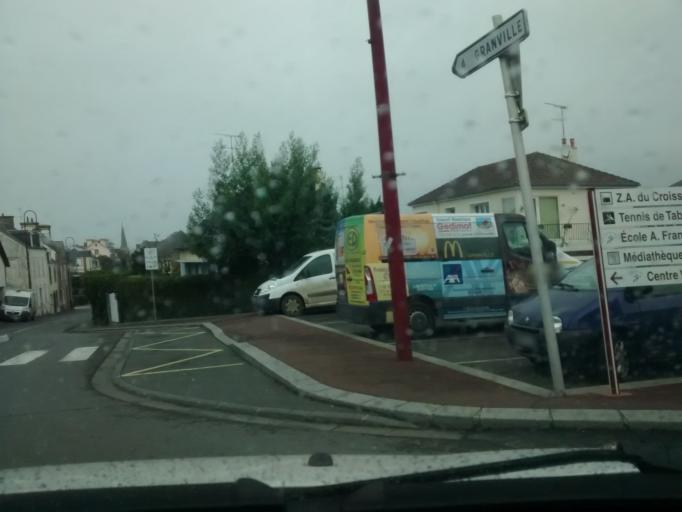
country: FR
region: Lower Normandy
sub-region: Departement de la Manche
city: Saint-Pair-sur-Mer
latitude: 48.8130
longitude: -1.5660
